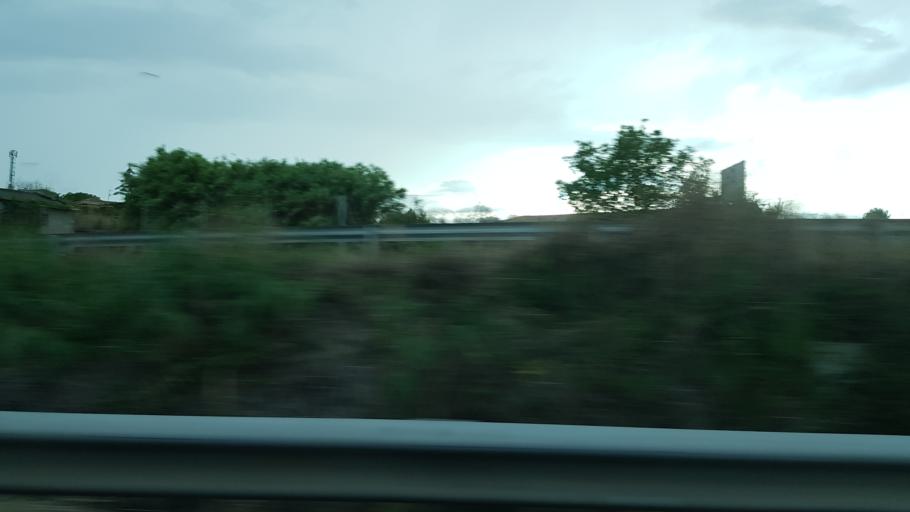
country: ES
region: La Rioja
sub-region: Provincia de La Rioja
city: Lardero
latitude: 42.4299
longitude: -2.4693
